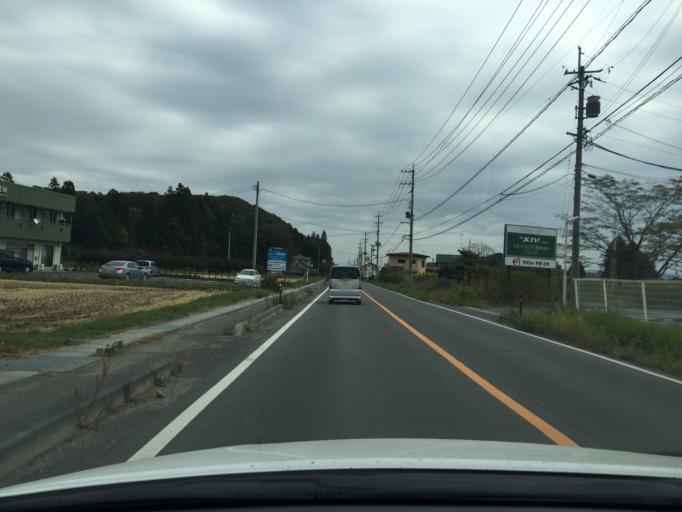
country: JP
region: Tochigi
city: Kuroiso
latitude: 37.1324
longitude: 140.1717
